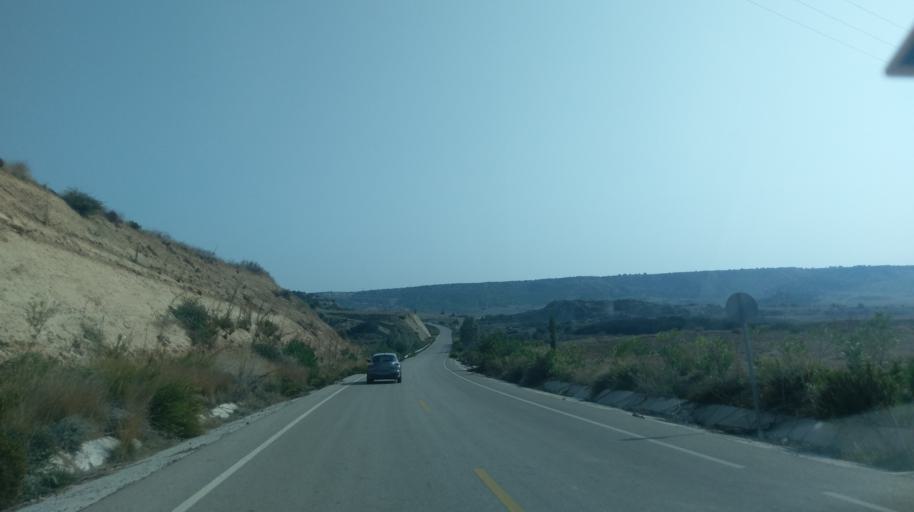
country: CY
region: Ammochostos
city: Leonarisso
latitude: 35.4800
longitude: 34.1114
